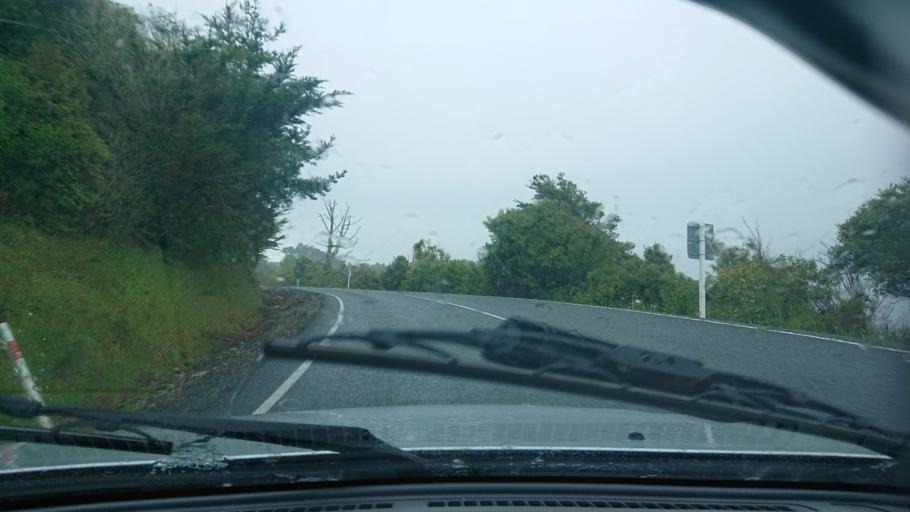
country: NZ
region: Auckland
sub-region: Auckland
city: Wellsford
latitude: -36.3093
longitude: 174.4875
